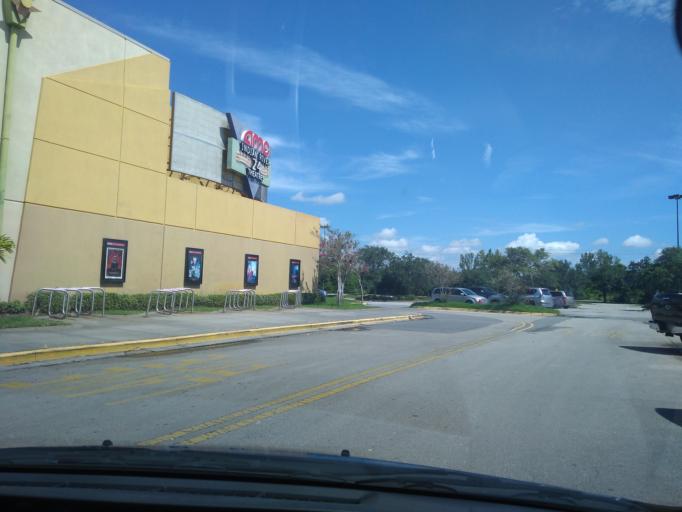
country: US
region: Florida
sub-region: Indian River County
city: West Vero Corridor
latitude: 27.6435
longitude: -80.4589
